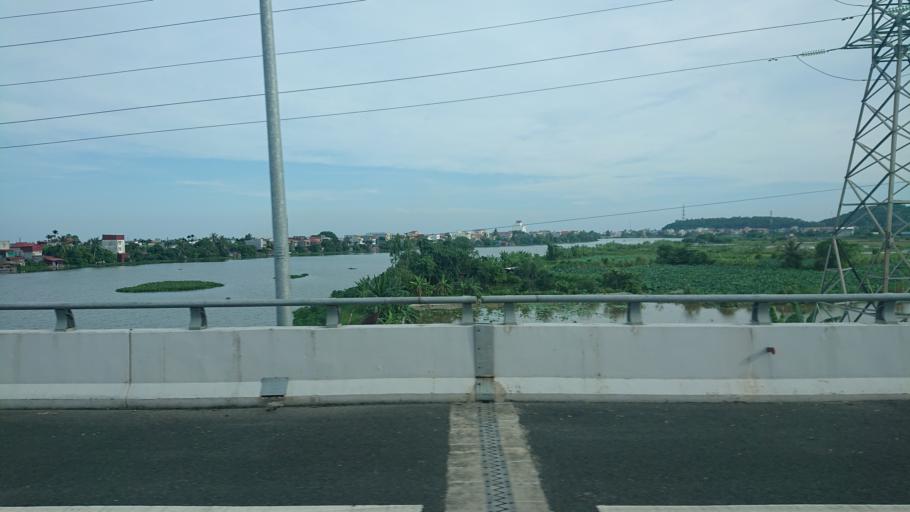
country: VN
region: Hai Phong
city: Nui Doi
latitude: 20.7654
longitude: 106.6743
